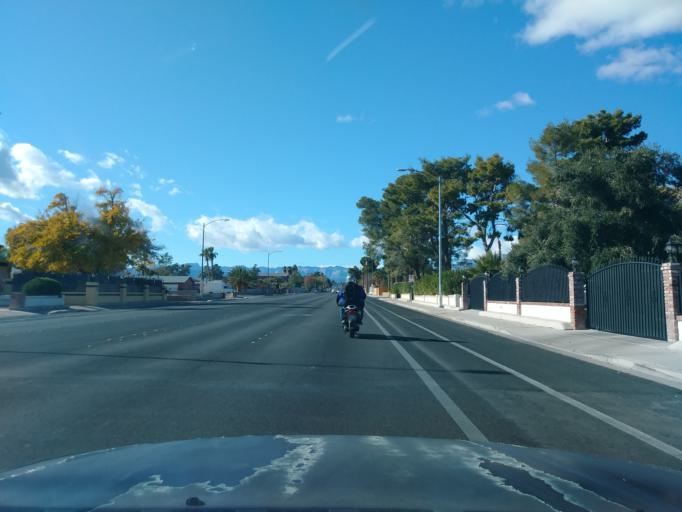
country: US
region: Nevada
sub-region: Clark County
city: Spring Valley
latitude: 36.1518
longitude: -115.2200
